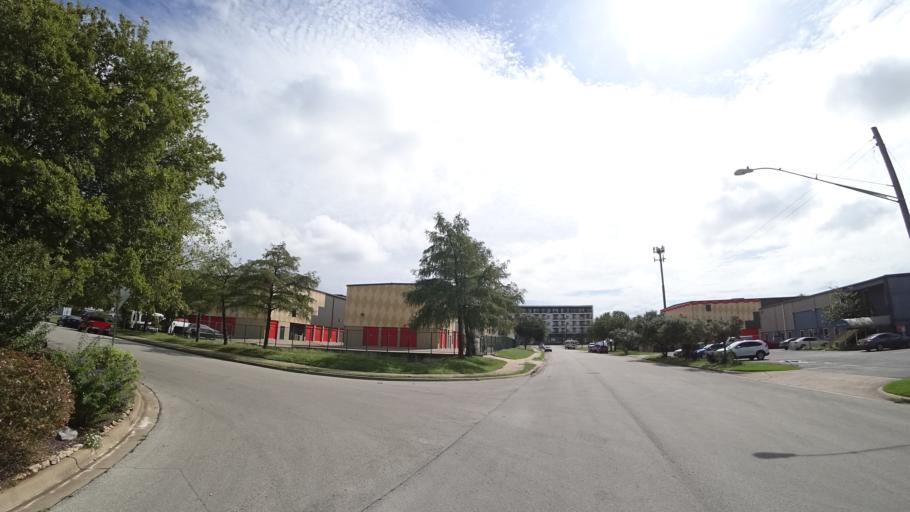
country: US
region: Texas
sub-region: Travis County
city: Austin
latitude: 30.3426
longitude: -97.7403
